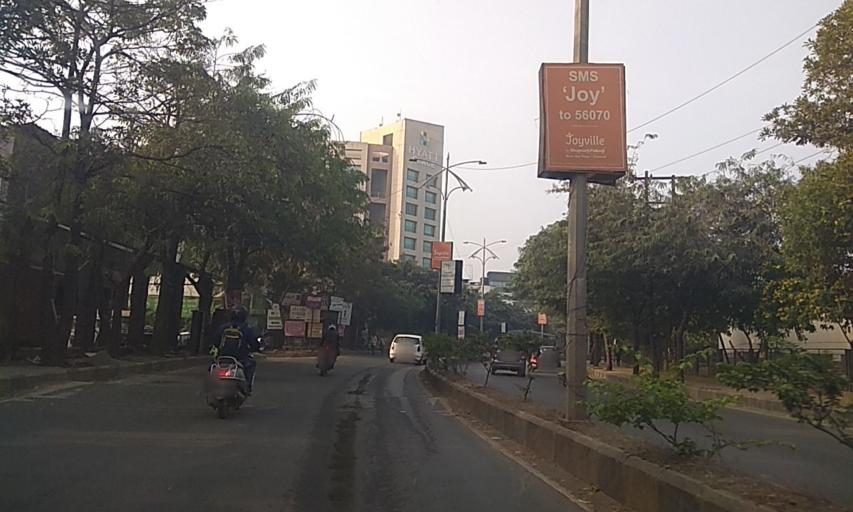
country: IN
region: Maharashtra
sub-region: Pune Division
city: Pimpri
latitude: 18.5870
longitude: 73.7368
